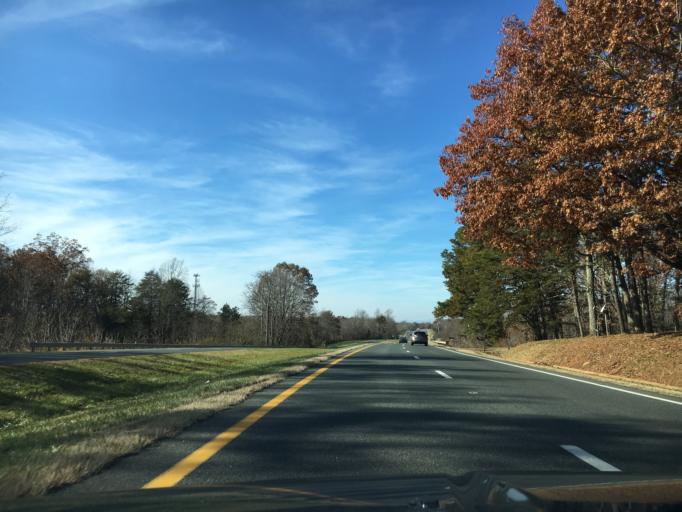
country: US
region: Virginia
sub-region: Campbell County
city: Concord
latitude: 37.3466
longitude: -78.9269
